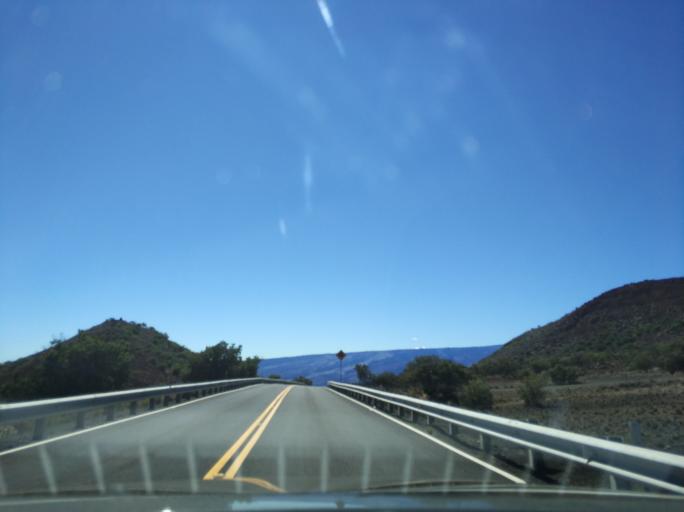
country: US
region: Hawaii
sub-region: Hawaii County
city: Honoka'a
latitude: 19.7580
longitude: -155.4563
